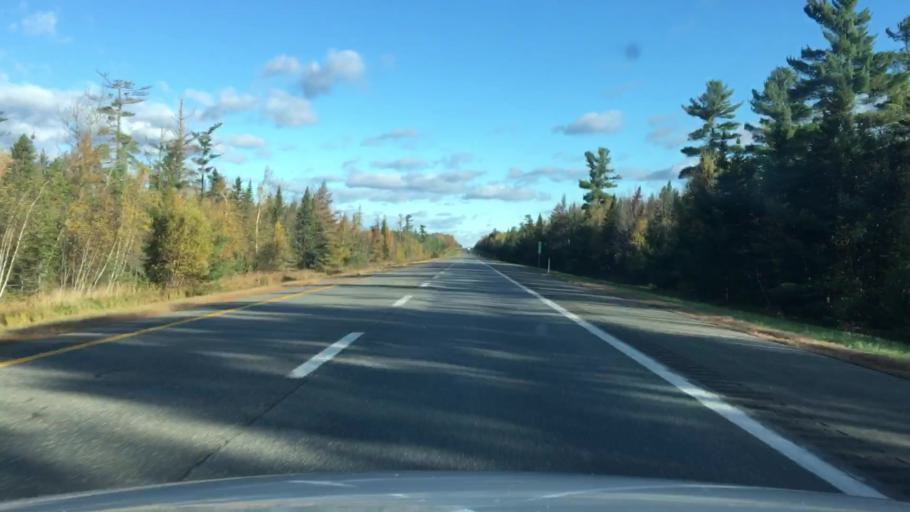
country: US
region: Maine
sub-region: Penobscot County
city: Greenbush
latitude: 45.0584
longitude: -68.6880
